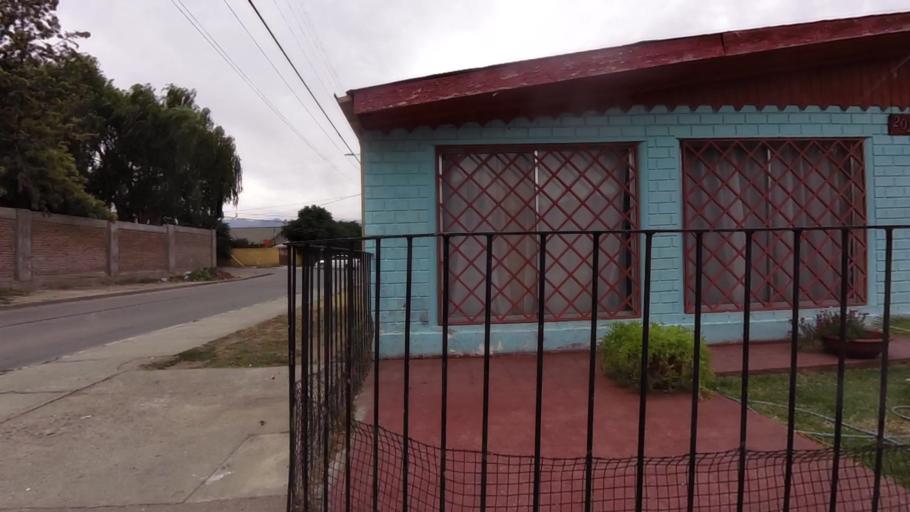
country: CL
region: O'Higgins
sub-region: Provincia de Cachapoal
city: Graneros
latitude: -34.0715
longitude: -70.7219
